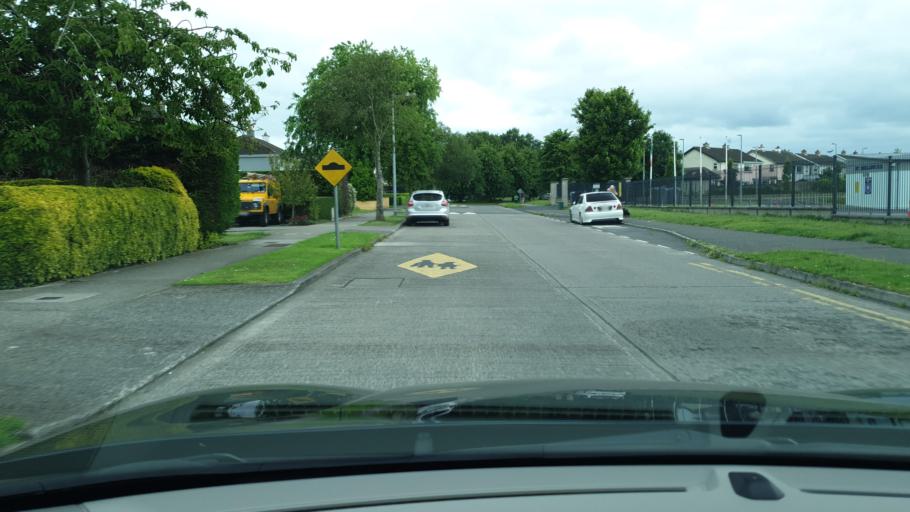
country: IE
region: Leinster
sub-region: An Mhi
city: Ashbourne
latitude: 53.5059
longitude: -6.3998
